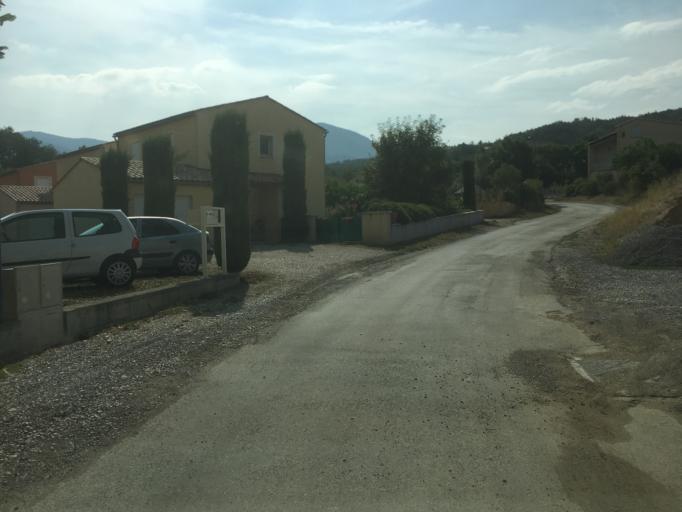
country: FR
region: Provence-Alpes-Cote d'Azur
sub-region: Departement des Alpes-de-Haute-Provence
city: Mallemoisson
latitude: 43.9398
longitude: 6.1716
